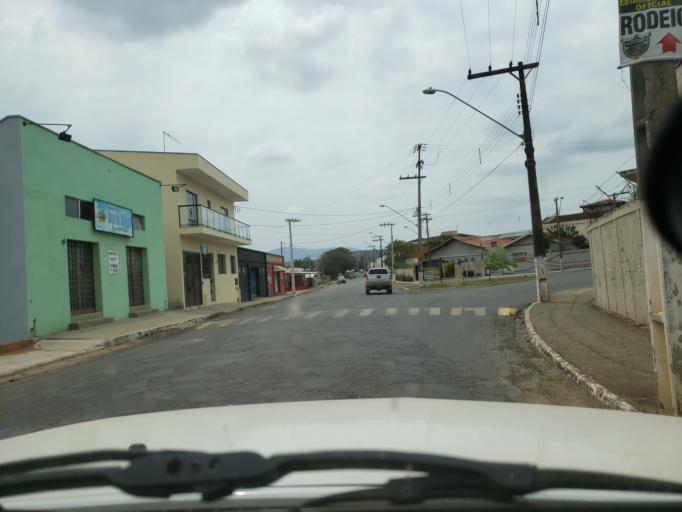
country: BR
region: Minas Gerais
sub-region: Jacutinga
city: Jacutinga
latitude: -22.2795
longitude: -46.6071
